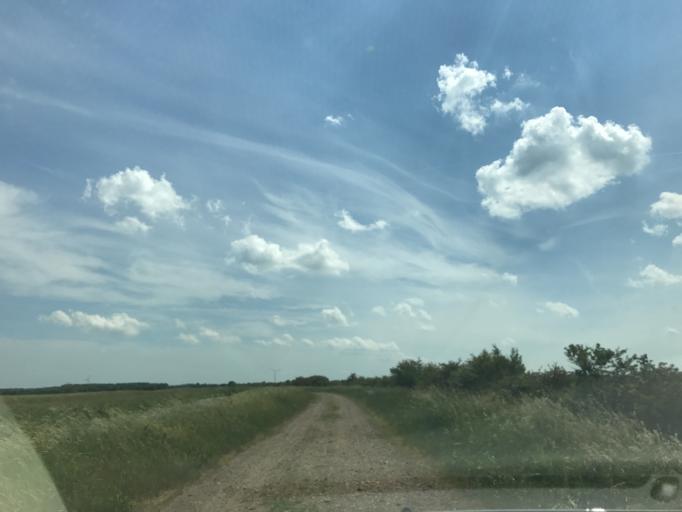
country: DE
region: Schleswig-Holstein
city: Ellhoft
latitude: 54.9251
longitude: 8.9367
